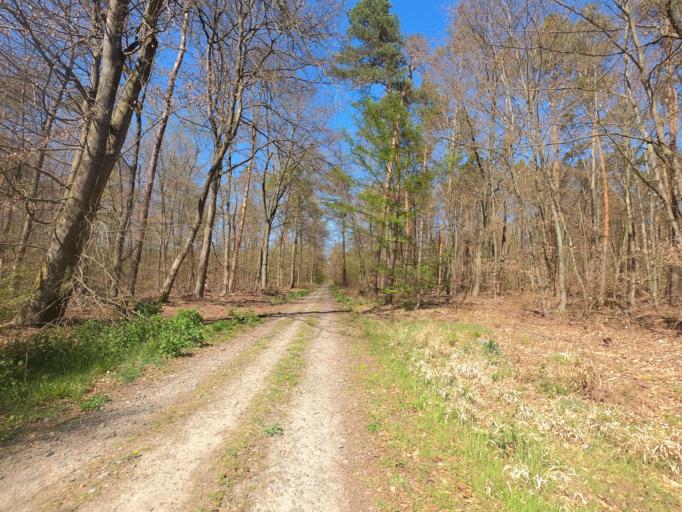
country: DE
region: Hesse
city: Morfelden-Walldorf
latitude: 49.9536
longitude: 8.5726
